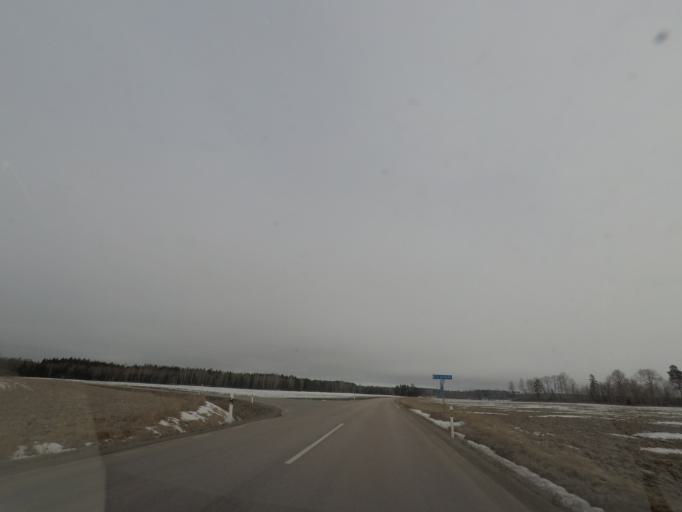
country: SE
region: Vaestmanland
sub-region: Vasteras
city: Skultuna
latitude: 59.7361
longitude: 16.4127
